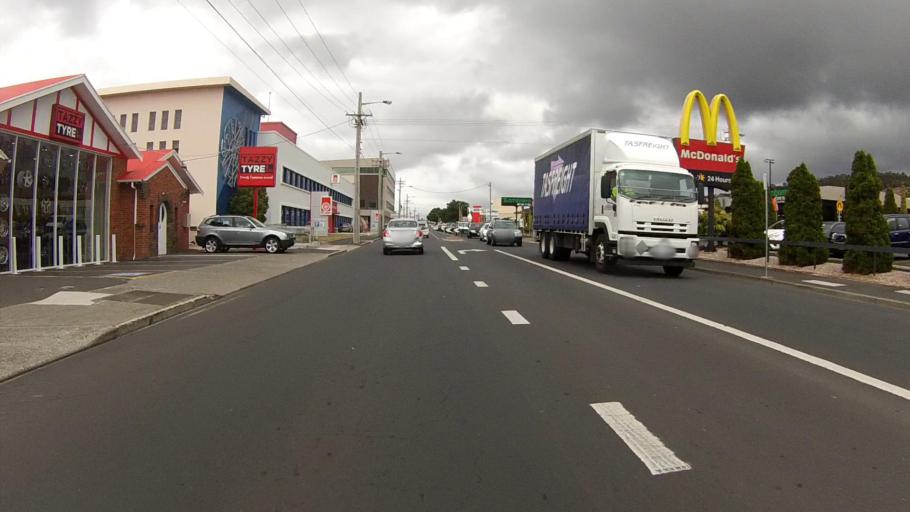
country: AU
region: Tasmania
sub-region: Glenorchy
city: Moonah
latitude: -42.8414
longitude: 147.2912
